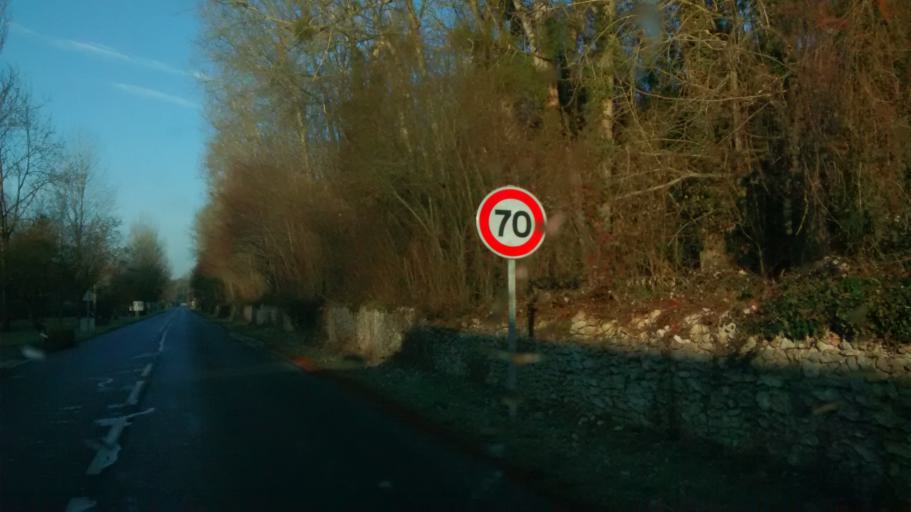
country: FR
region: Centre
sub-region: Departement d'Indre-et-Loire
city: Esvres
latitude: 47.2855
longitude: 0.7779
